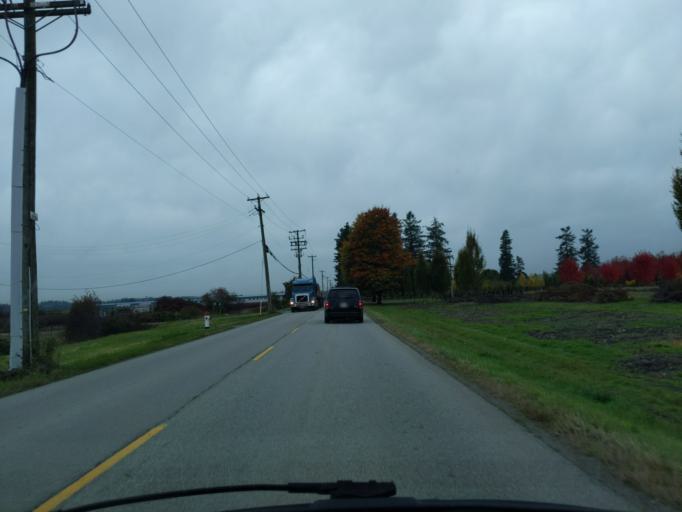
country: CA
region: British Columbia
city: Pitt Meadows
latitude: 49.2225
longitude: -122.7082
